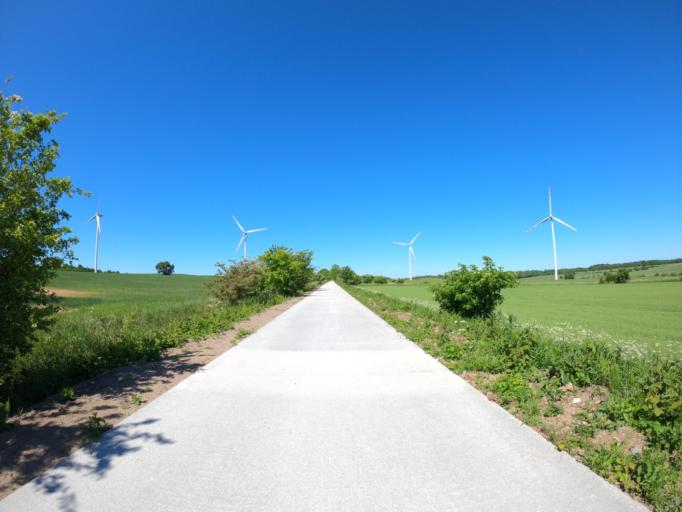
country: PL
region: Pomeranian Voivodeship
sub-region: Powiat slupski
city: Ustka
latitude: 54.5130
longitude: 16.7531
